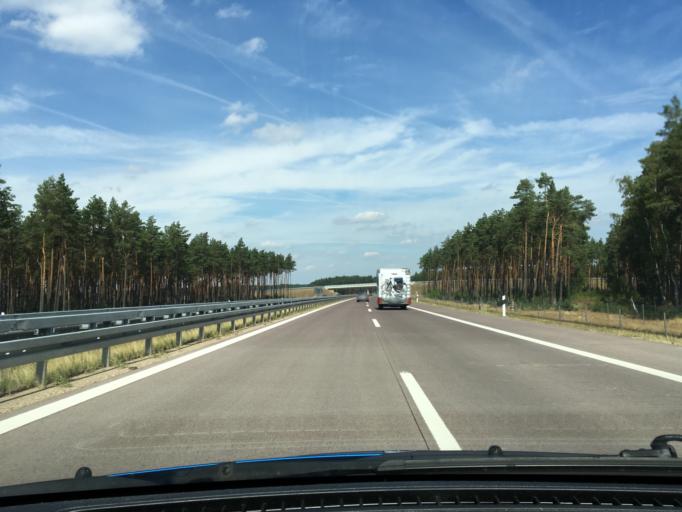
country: DE
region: Mecklenburg-Vorpommern
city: Ludwigslust
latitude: 53.3552
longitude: 11.5159
